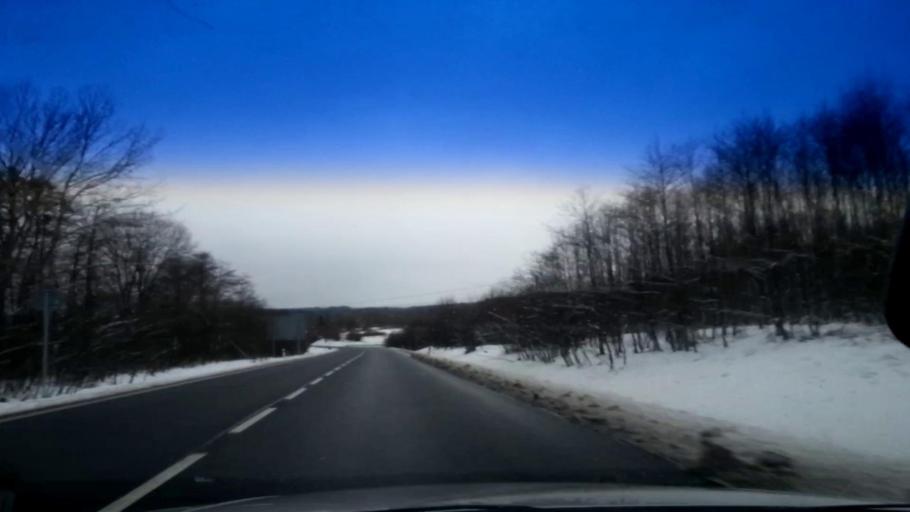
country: CZ
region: Karlovarsky
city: As
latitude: 50.1944
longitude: 12.2153
